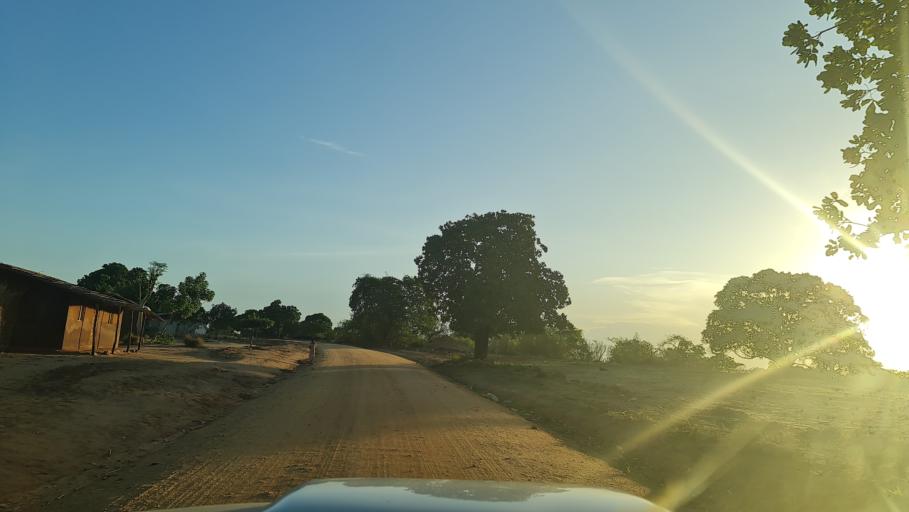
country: MZ
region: Nampula
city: Ilha de Mocambique
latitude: -14.8924
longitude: 40.3125
